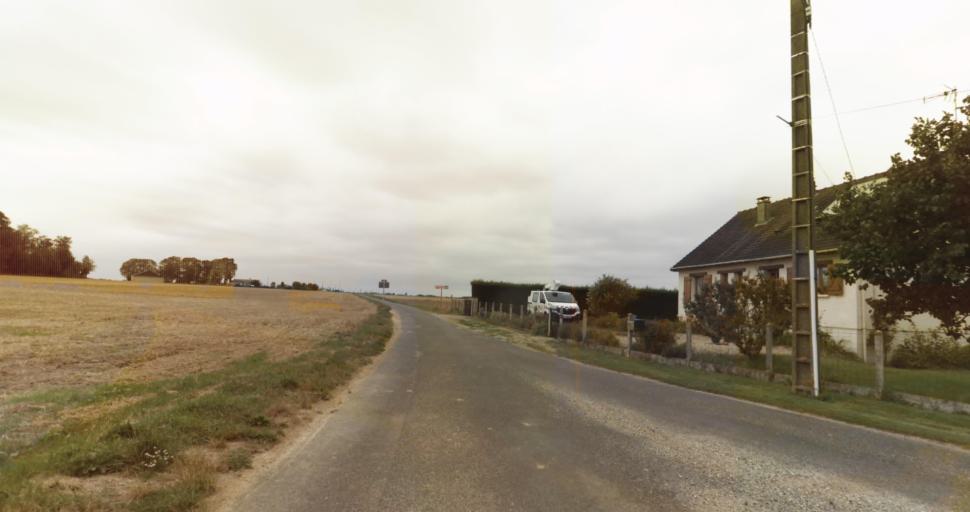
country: FR
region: Haute-Normandie
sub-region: Departement de l'Eure
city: Marcilly-sur-Eure
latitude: 48.9083
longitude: 1.3080
